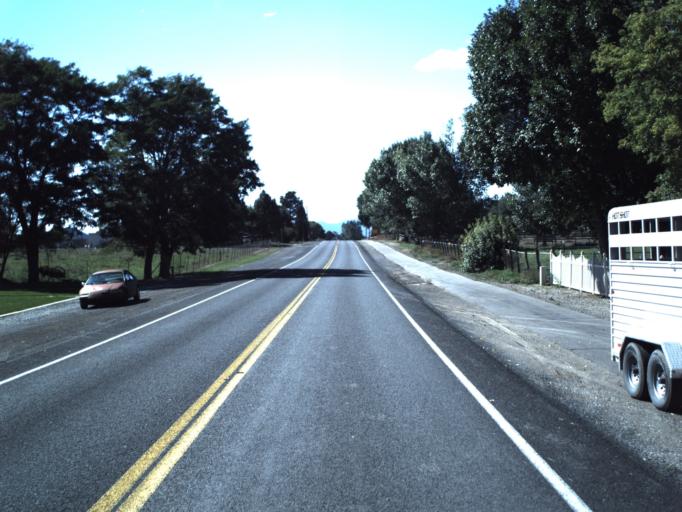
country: US
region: Utah
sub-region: Beaver County
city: Beaver
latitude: 38.2768
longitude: -112.6116
